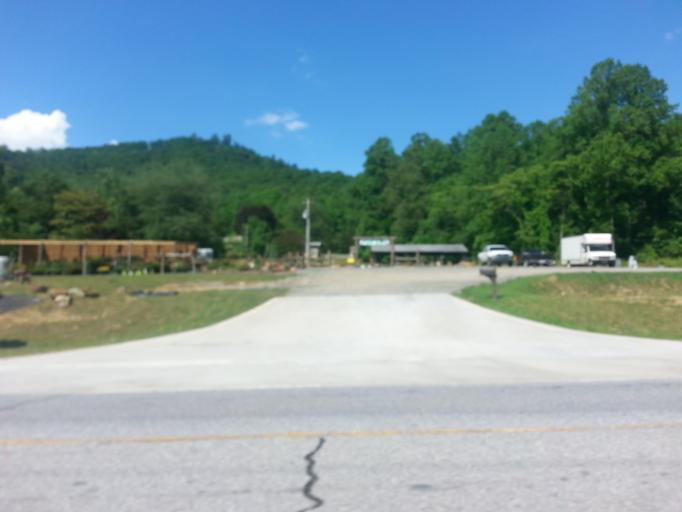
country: US
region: Georgia
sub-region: Towns County
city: Hiawassee
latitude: 34.9417
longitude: -83.7489
